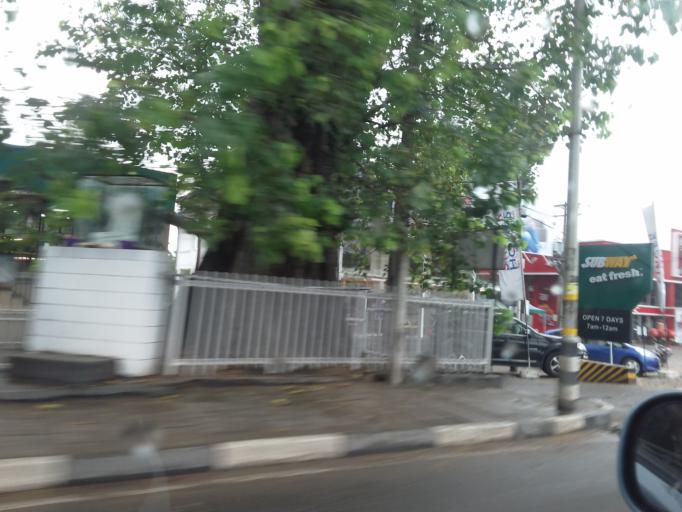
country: LK
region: Western
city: Pita Kotte
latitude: 6.9063
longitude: 79.9035
